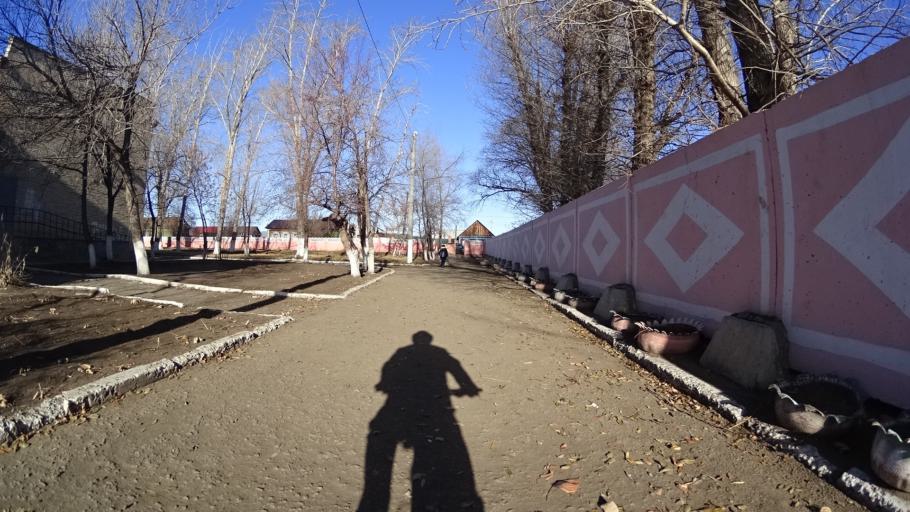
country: RU
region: Chelyabinsk
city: Troitsk
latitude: 54.0909
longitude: 61.5895
